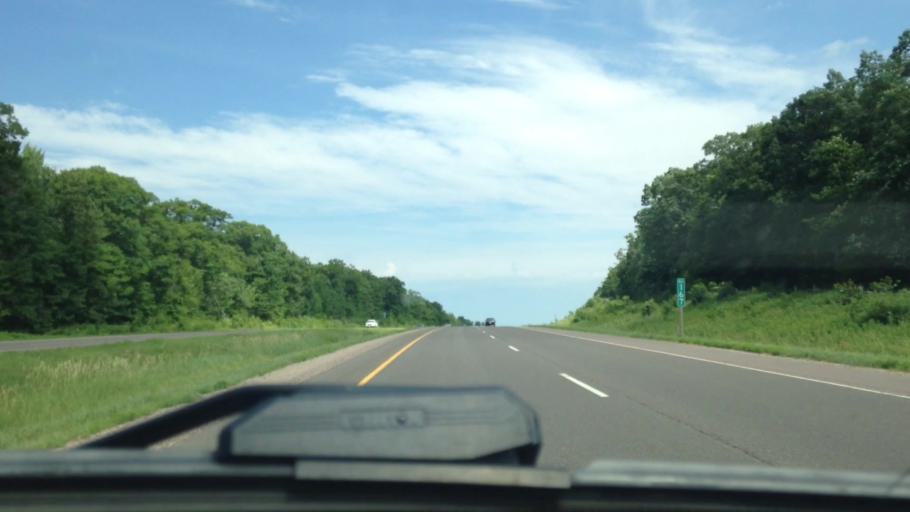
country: US
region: Wisconsin
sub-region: Washburn County
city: Spooner
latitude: 45.8326
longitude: -91.8588
